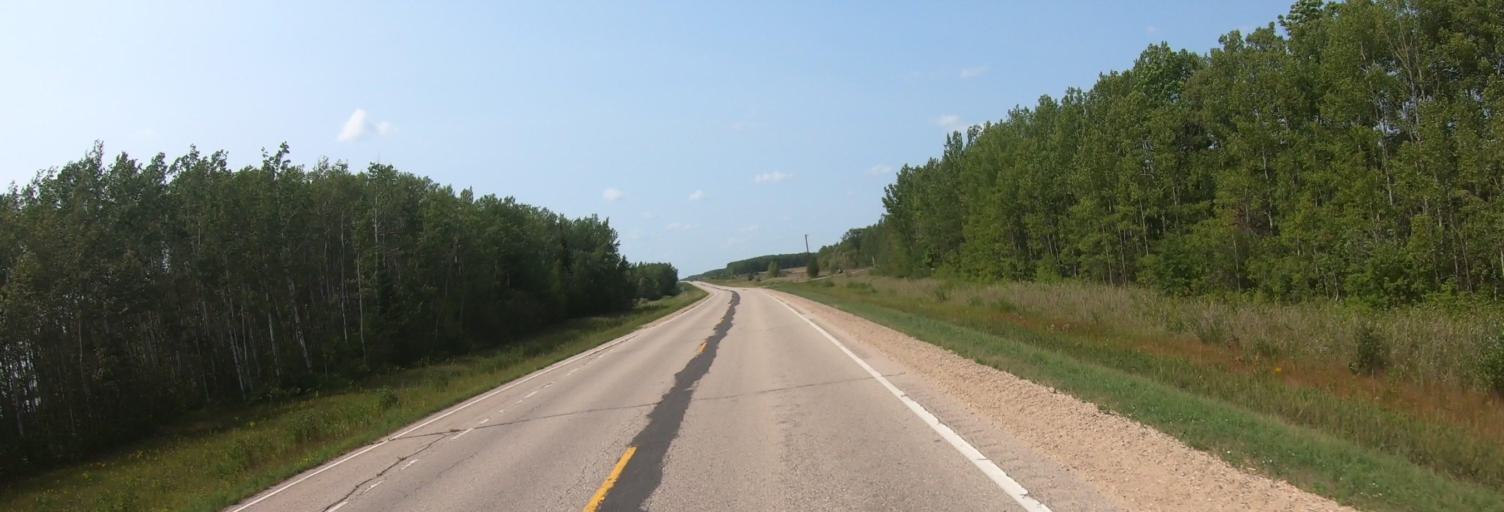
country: US
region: Minnesota
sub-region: Lake of the Woods County
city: Baudette
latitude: 48.7439
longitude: -94.8542
